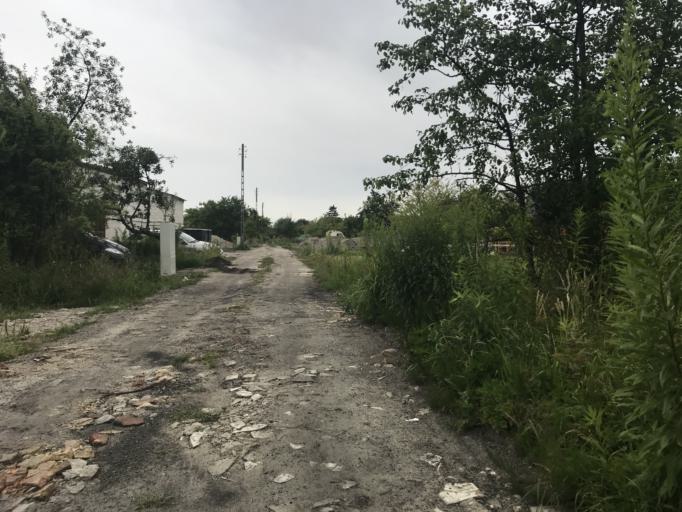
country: PL
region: Pomeranian Voivodeship
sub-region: Gdansk
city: Gdansk
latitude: 54.3383
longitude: 18.6788
